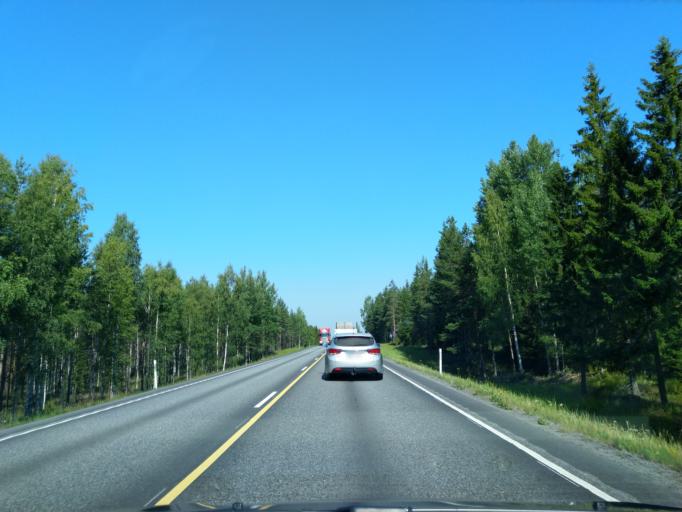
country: FI
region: Satakunta
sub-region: Pori
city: Huittinen
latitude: 61.1264
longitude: 22.8022
